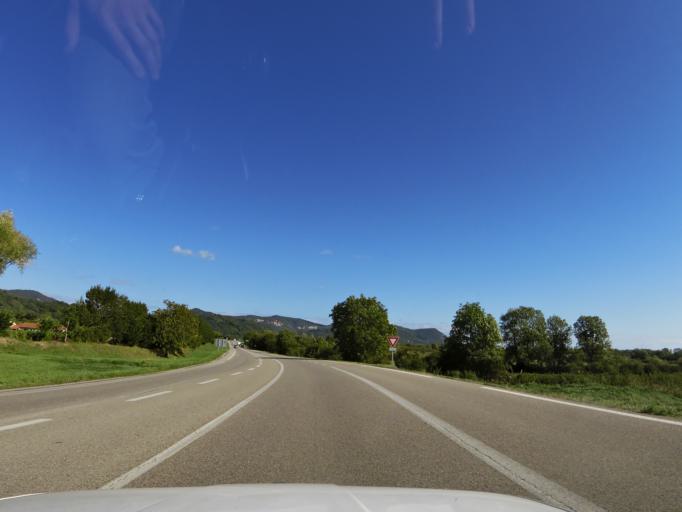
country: FR
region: Rhone-Alpes
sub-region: Departement de l'Ain
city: Saint-Denis-en-Bugey
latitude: 45.9458
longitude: 5.3203
